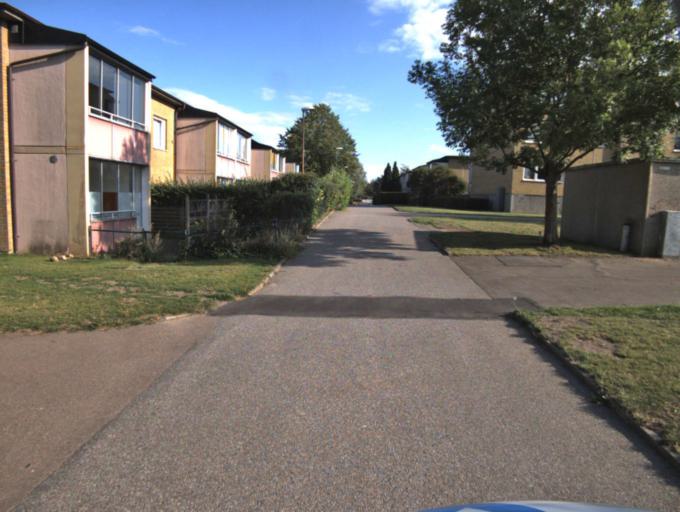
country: SE
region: Skane
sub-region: Kavlinge Kommun
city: Kaevlinge
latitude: 55.7960
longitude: 13.1043
